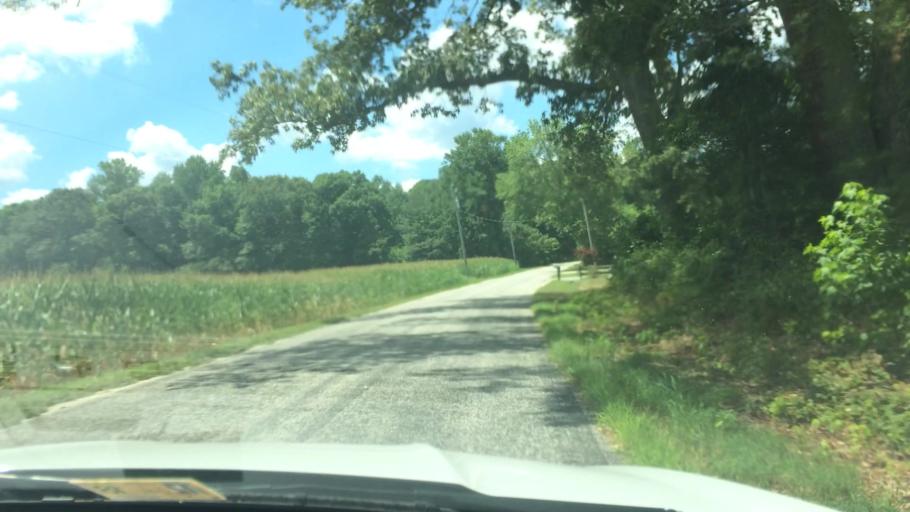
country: US
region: Virginia
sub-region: King William County
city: West Point
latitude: 37.6038
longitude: -76.7843
